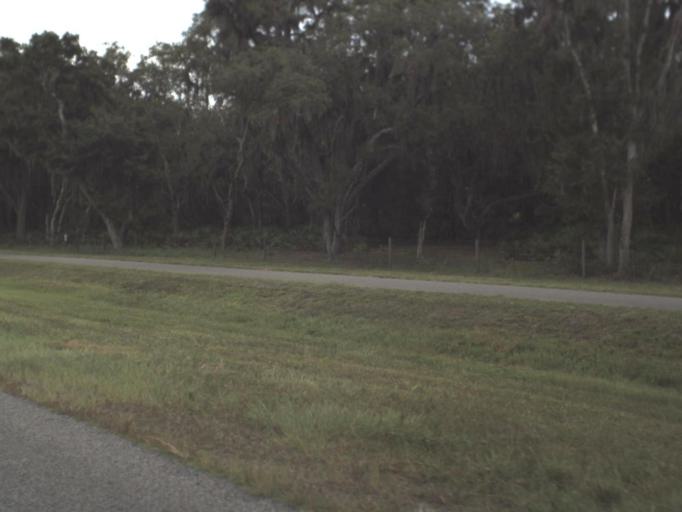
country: US
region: Florida
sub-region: Pasco County
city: Wesley Chapel
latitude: 28.1977
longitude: -82.3067
